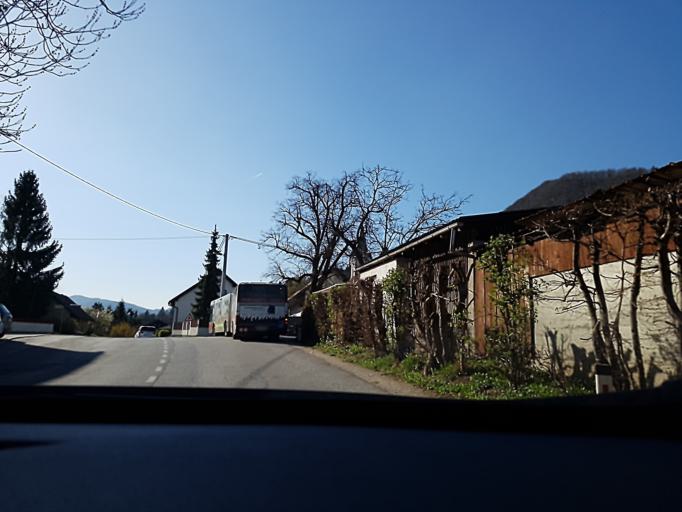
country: SI
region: Medvode
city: Zgornje Pirnice
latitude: 46.1202
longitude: 14.4673
